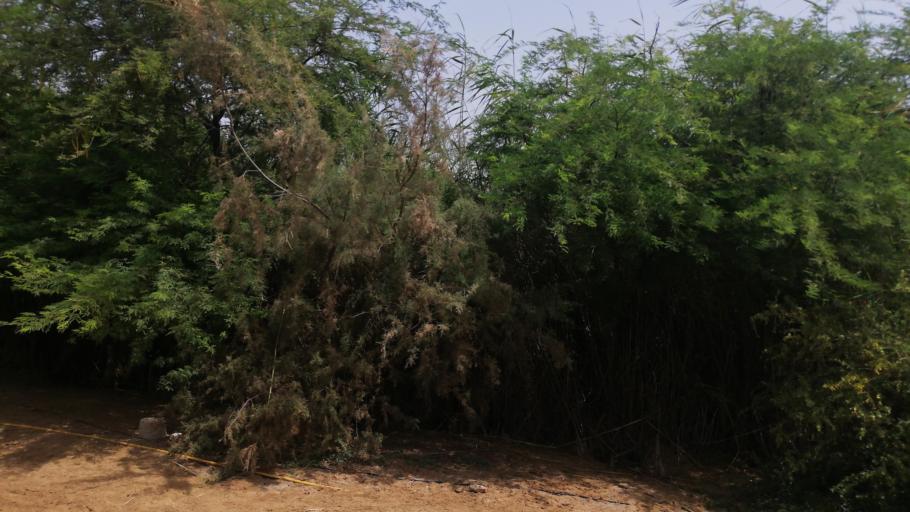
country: SN
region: Saint-Louis
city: Saint-Louis
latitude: 16.3603
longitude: -16.2748
